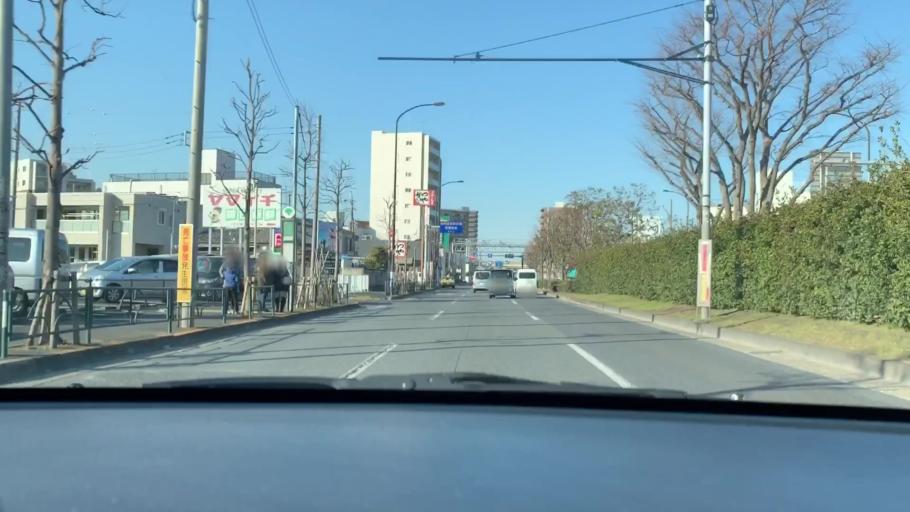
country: JP
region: Tokyo
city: Urayasu
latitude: 35.6909
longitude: 139.8827
